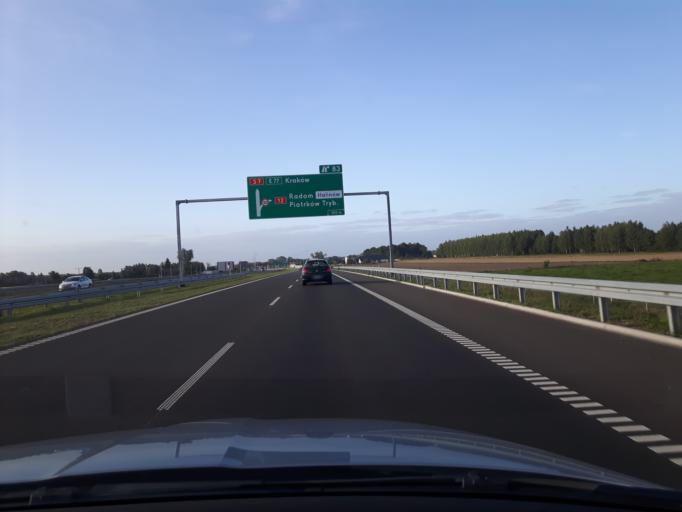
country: PL
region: Masovian Voivodeship
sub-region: Powiat radomski
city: Zakrzew
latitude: 51.3986
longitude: 21.0241
